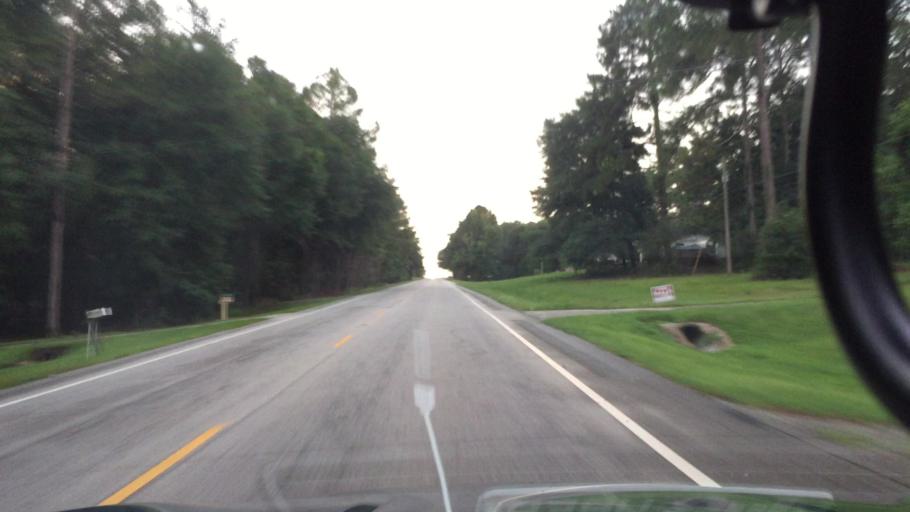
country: US
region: Alabama
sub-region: Coffee County
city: New Brockton
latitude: 31.4375
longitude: -85.8916
